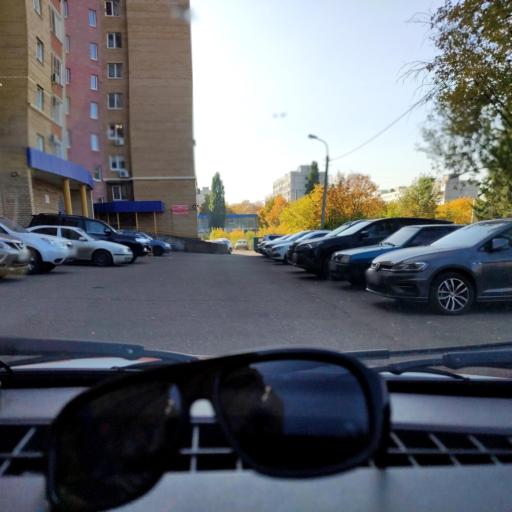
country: RU
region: Bashkortostan
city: Ufa
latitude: 54.7255
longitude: 56.0136
